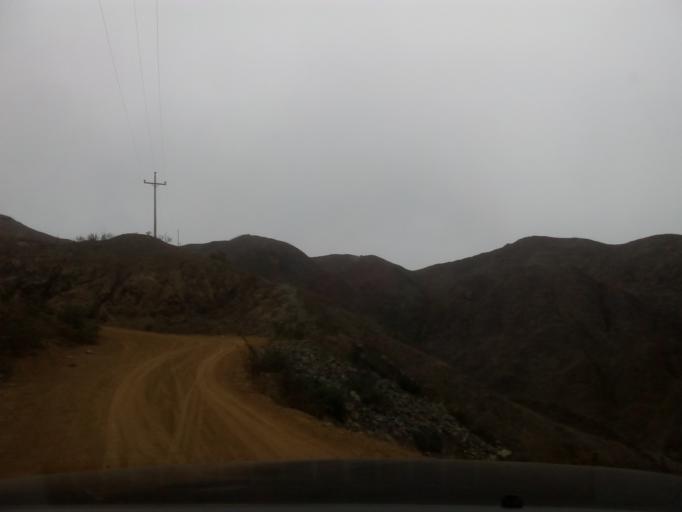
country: PE
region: La Libertad
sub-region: Viru
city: Viru
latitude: -8.3638
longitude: -78.6438
